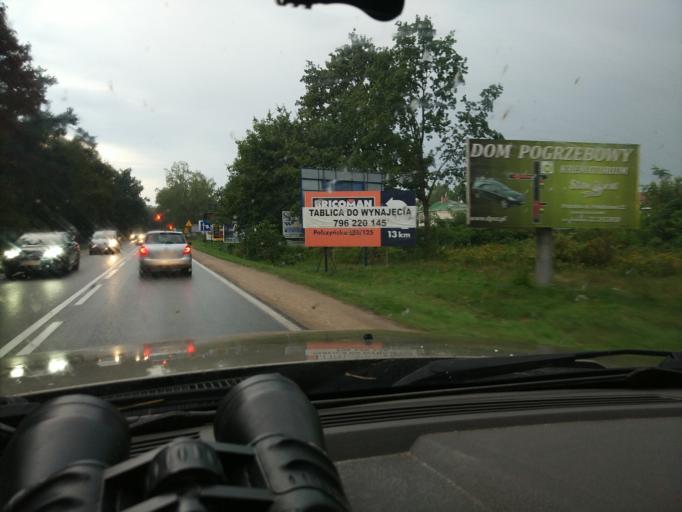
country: PL
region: Masovian Voivodeship
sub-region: Powiat pruszkowski
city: Granica
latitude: 52.1487
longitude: 20.7899
